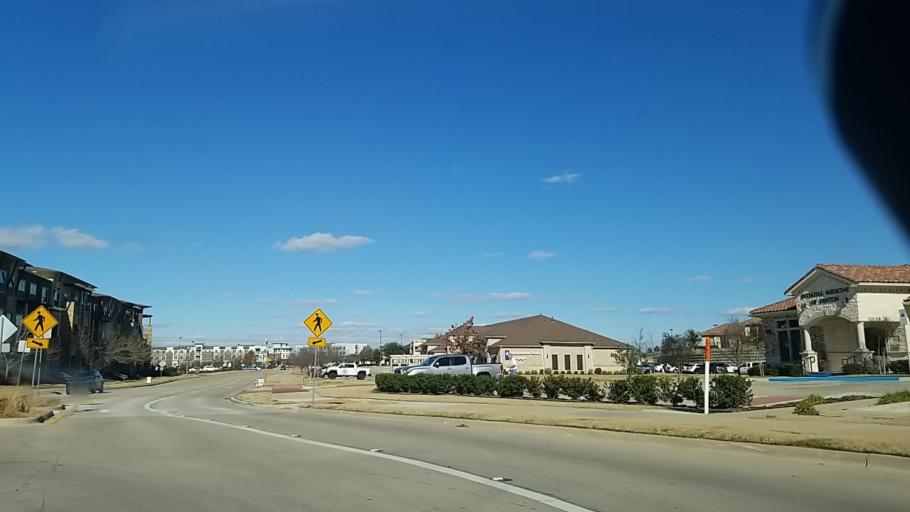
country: US
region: Texas
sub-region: Denton County
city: Corinth
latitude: 33.1732
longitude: -97.0964
